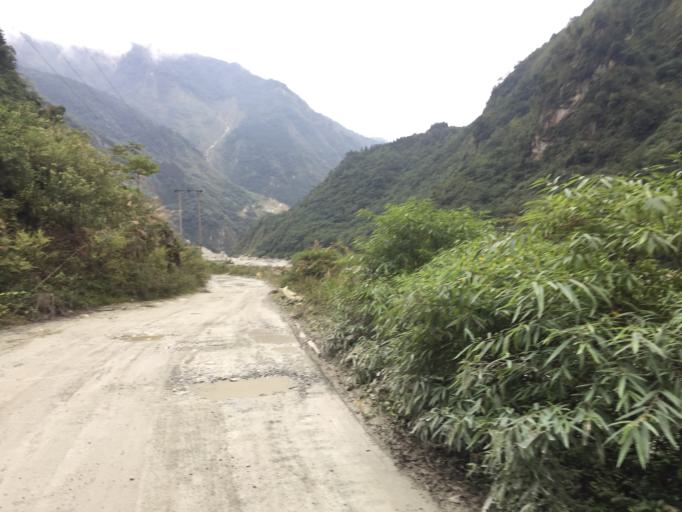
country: CN
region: Sichuan
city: Guangsheng
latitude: 31.0683
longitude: 103.4461
